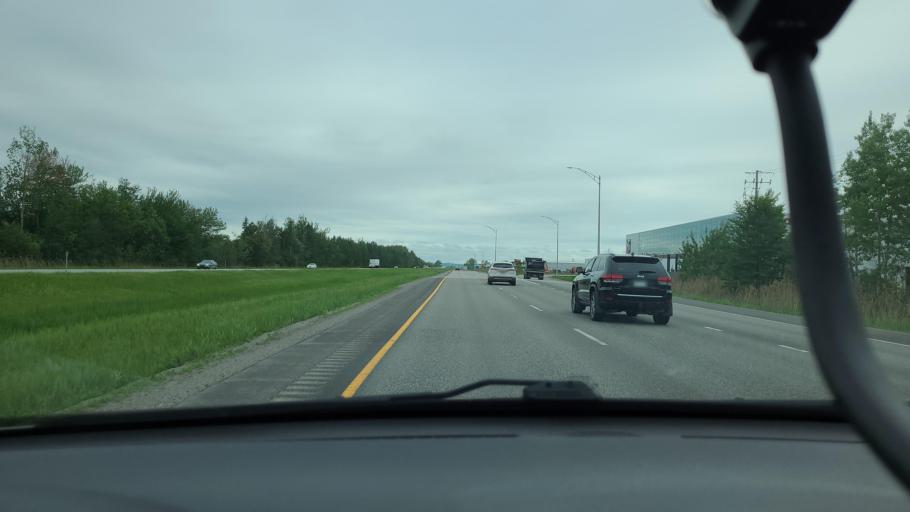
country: CA
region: Quebec
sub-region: Lanaudiere
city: Mascouche
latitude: 45.8220
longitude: -73.6041
